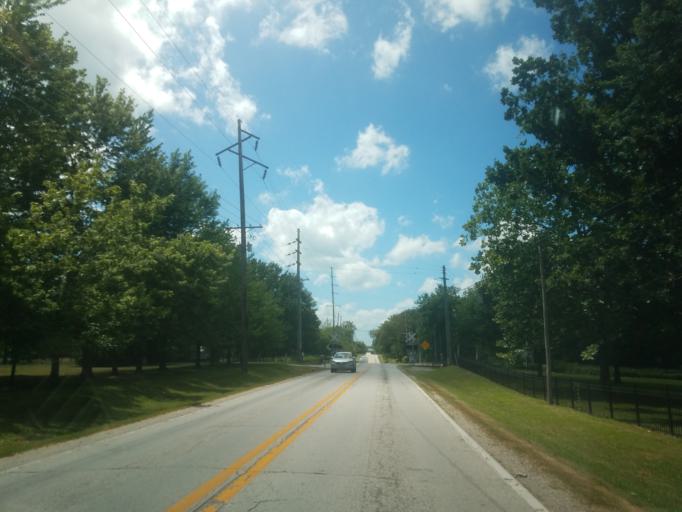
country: US
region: Illinois
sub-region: McLean County
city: Bloomington
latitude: 40.4589
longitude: -89.0191
